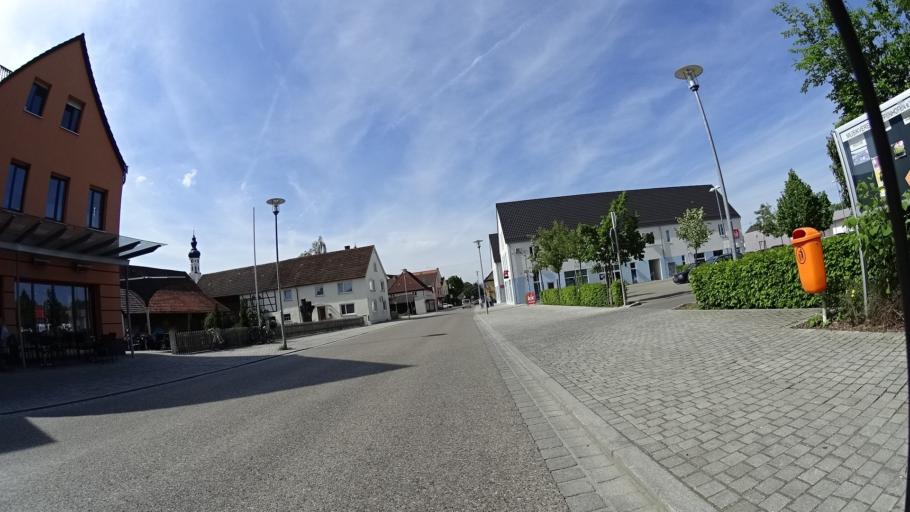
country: DE
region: Bavaria
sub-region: Swabia
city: Pfaffenhofen an der Roth
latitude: 48.3536
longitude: 10.1611
